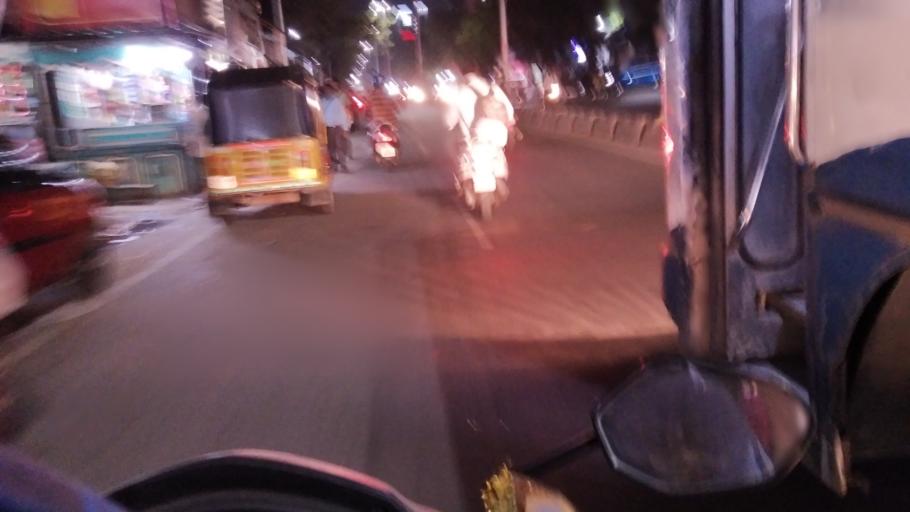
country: IN
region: Telangana
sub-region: Hyderabad
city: Malkajgiri
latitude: 17.4358
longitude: 78.4886
